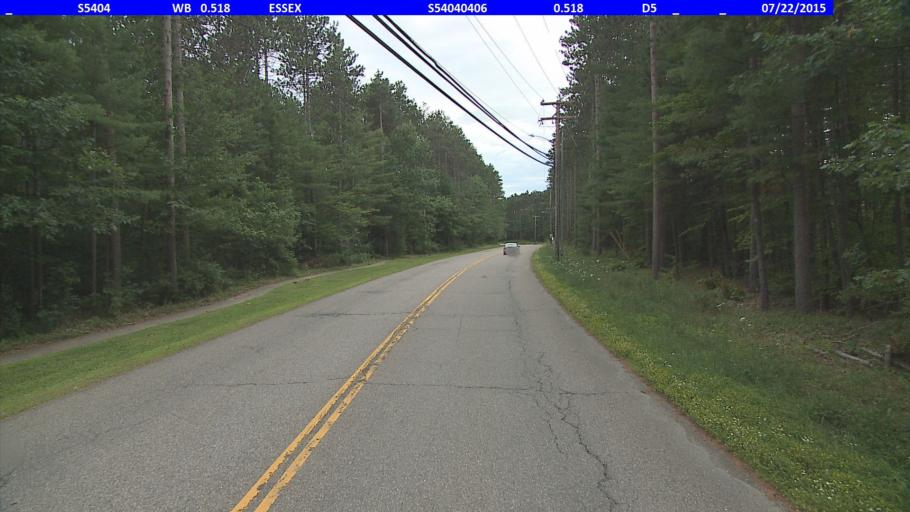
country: US
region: Vermont
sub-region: Chittenden County
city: Jericho
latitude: 44.4998
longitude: -73.0429
